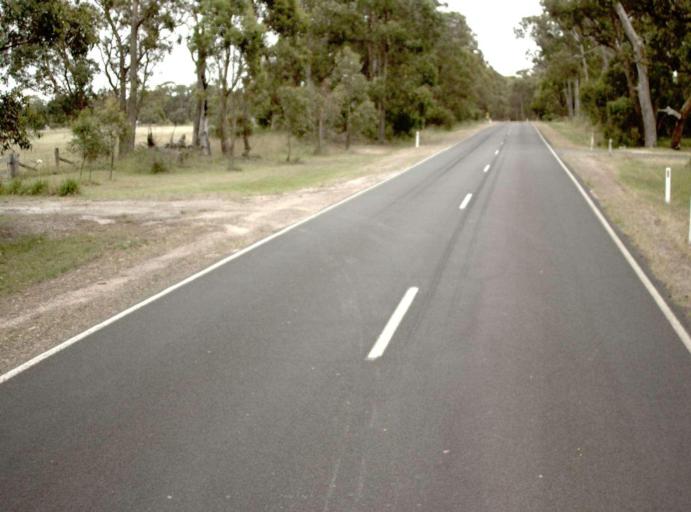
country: AU
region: Victoria
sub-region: Latrobe
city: Traralgon
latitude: -38.5187
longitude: 146.8581
